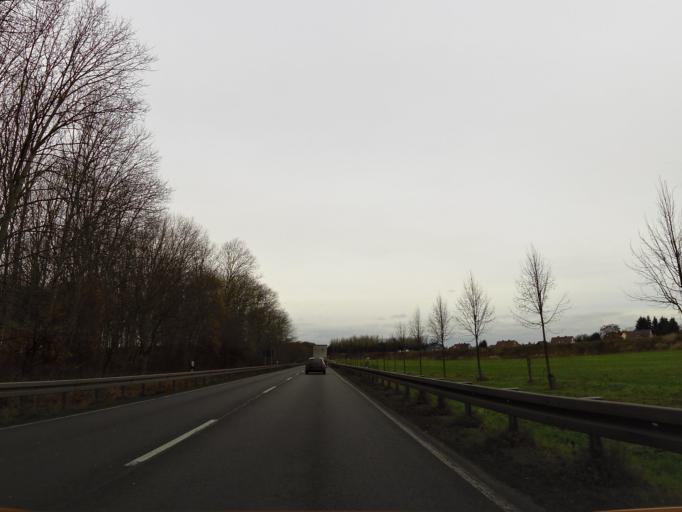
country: DE
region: Saxony-Anhalt
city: Salzwedel
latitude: 52.8331
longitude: 11.1847
